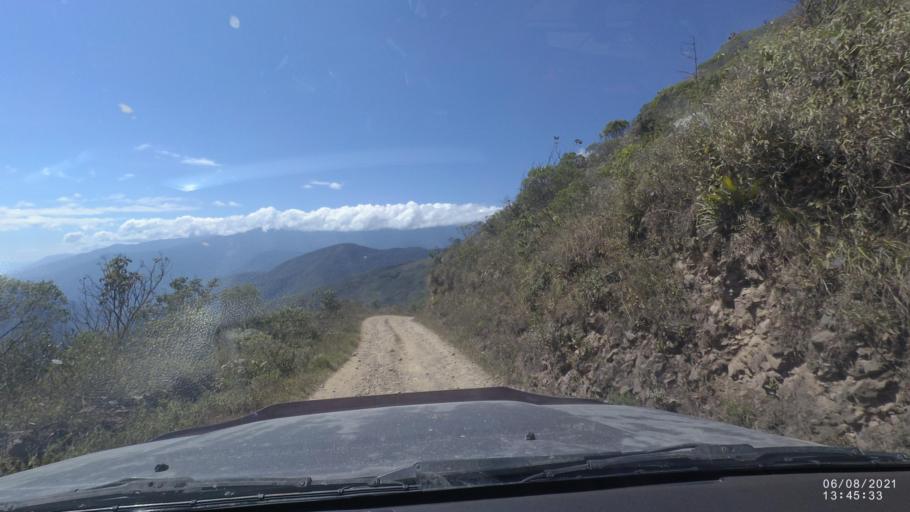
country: BO
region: La Paz
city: Quime
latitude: -16.6715
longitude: -66.7315
